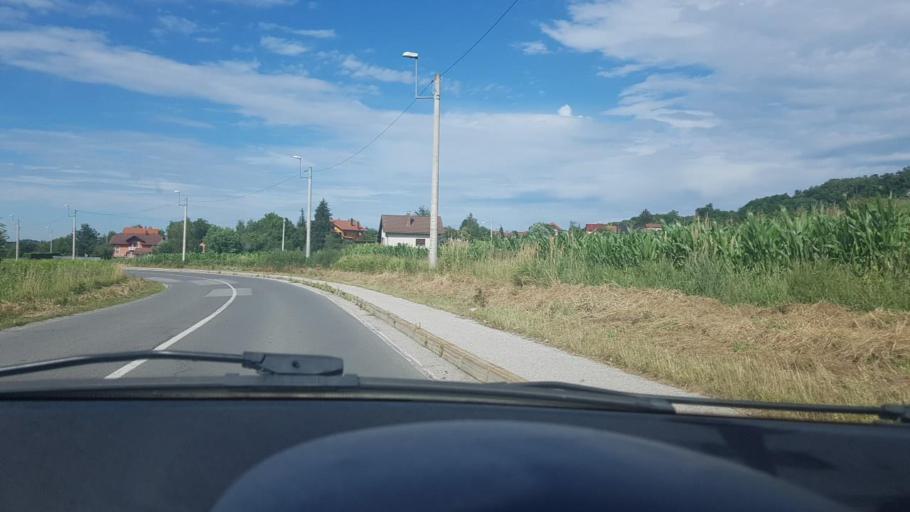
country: HR
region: Varazdinska
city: Lepoglava
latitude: 46.2135
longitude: 16.0632
